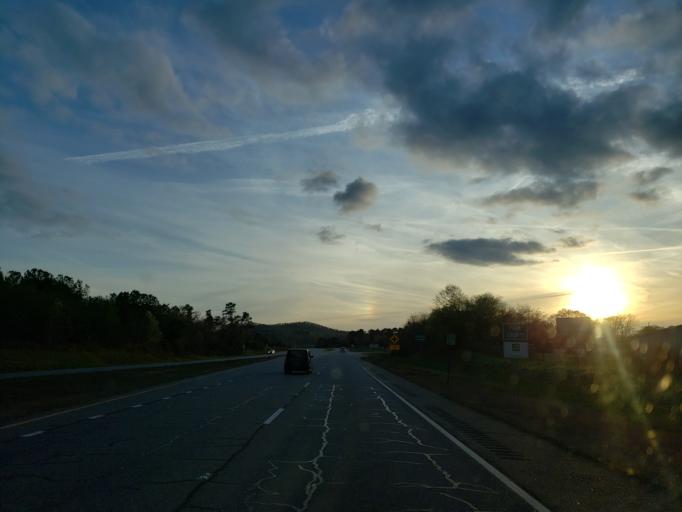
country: US
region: Georgia
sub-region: Bartow County
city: Euharlee
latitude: 34.0830
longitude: -84.9752
